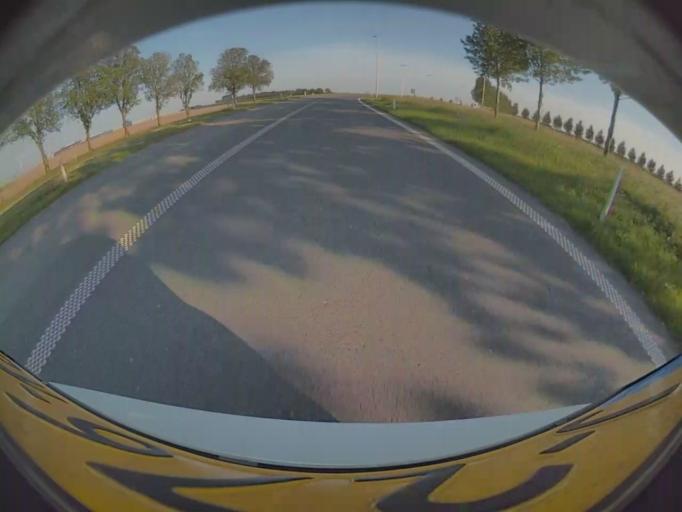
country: NL
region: North Brabant
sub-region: Gemeente Steenbergen
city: Dinteloord
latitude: 51.6250
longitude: 4.3842
